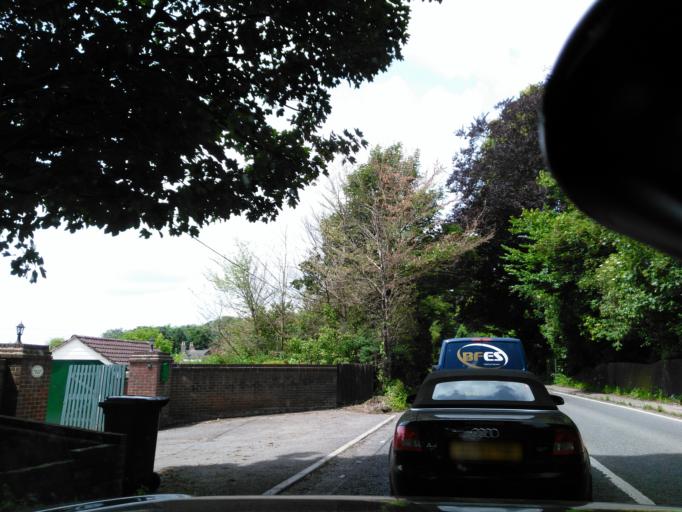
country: GB
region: England
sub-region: Wiltshire
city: Salisbury
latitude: 51.0612
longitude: -1.7657
